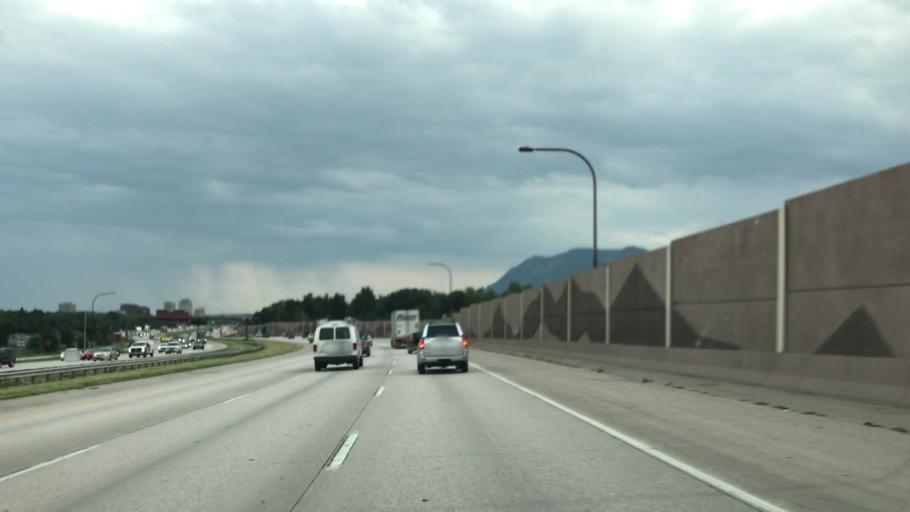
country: US
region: Colorado
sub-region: El Paso County
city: Colorado Springs
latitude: 38.8599
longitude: -104.8350
